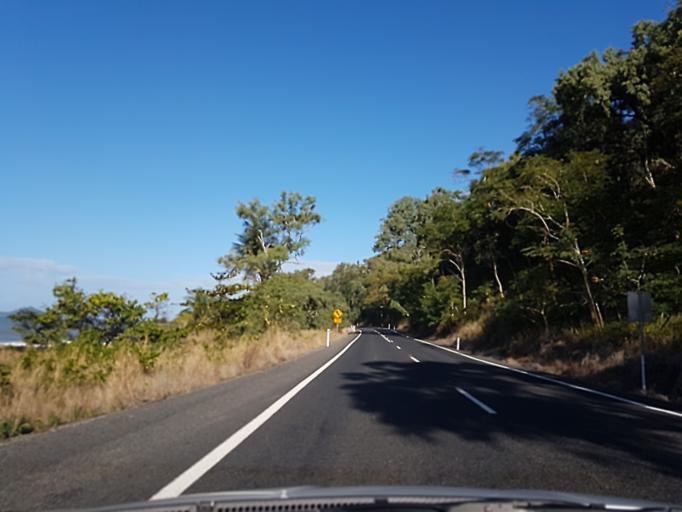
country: AU
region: Queensland
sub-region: Cairns
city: Palm Cove
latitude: -16.7105
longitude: 145.6321
